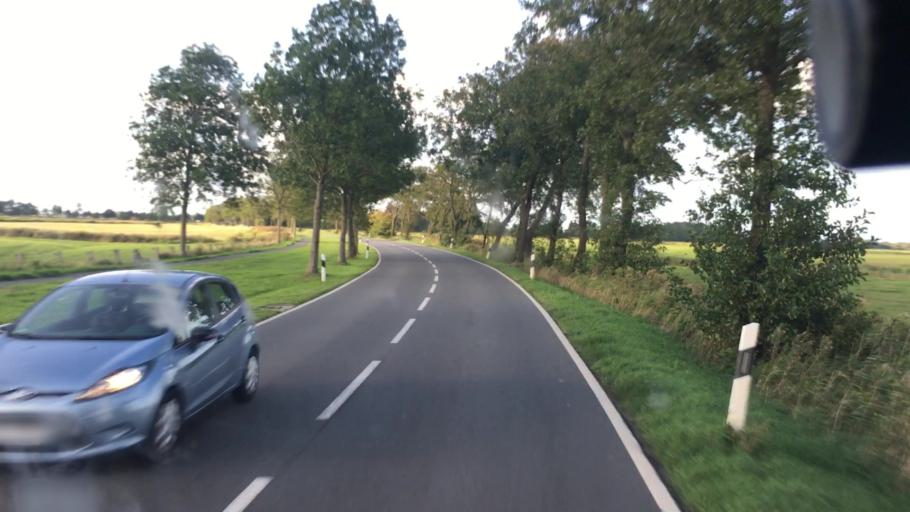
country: DE
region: Lower Saxony
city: Jever
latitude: 53.6002
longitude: 7.8699
